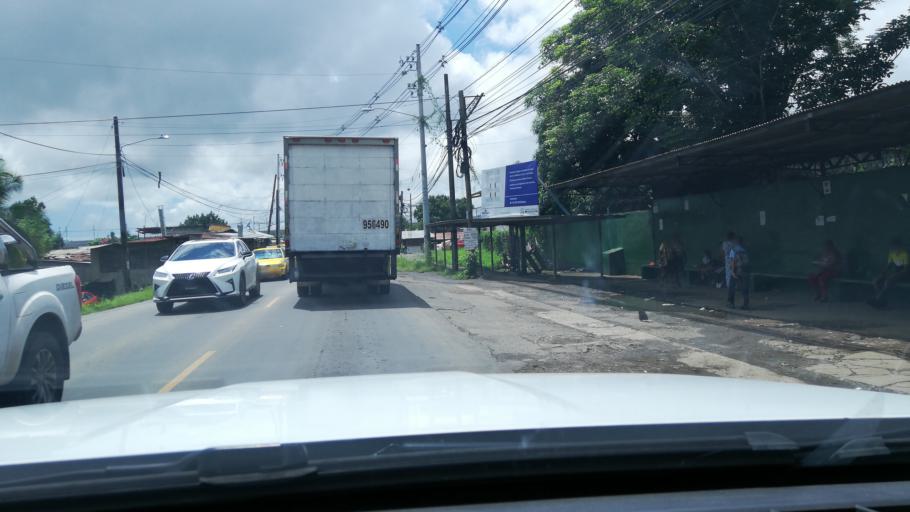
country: PA
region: Panama
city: Tocumen
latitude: 9.1052
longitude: -79.3628
